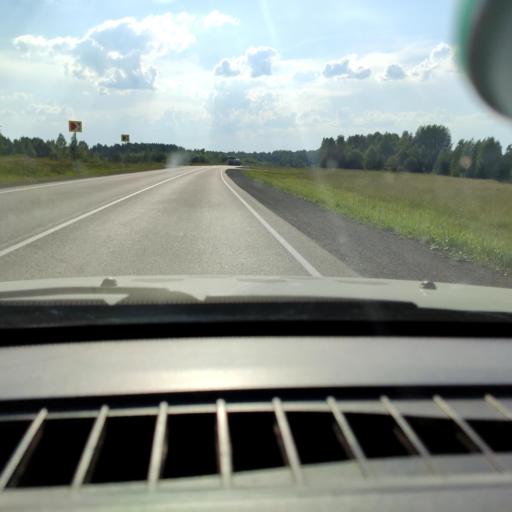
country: RU
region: Udmurtiya
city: Debesy
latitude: 57.7262
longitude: 54.1930
